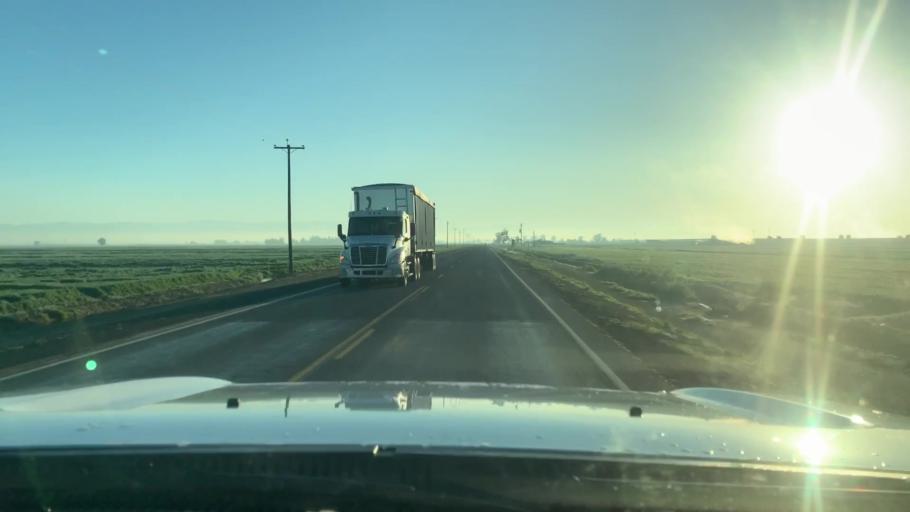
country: US
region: California
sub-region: Kings County
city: Home Garden
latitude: 36.2111
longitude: -119.6893
